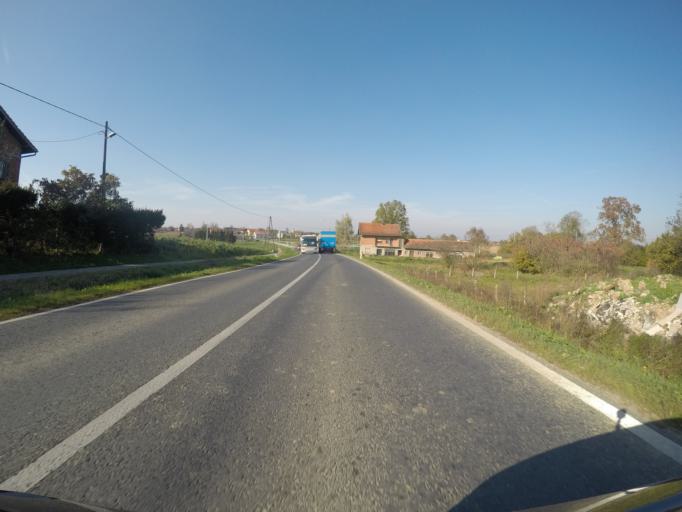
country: HR
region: Bjelovarsko-Bilogorska
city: Predavac
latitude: 45.9318
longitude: 16.7850
